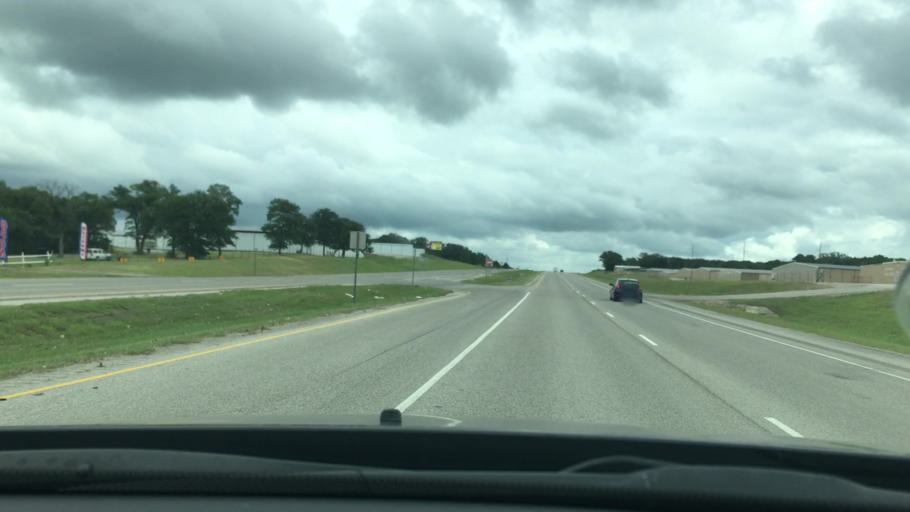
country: US
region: Oklahoma
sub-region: Carter County
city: Ardmore
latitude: 34.1342
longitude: -97.1001
